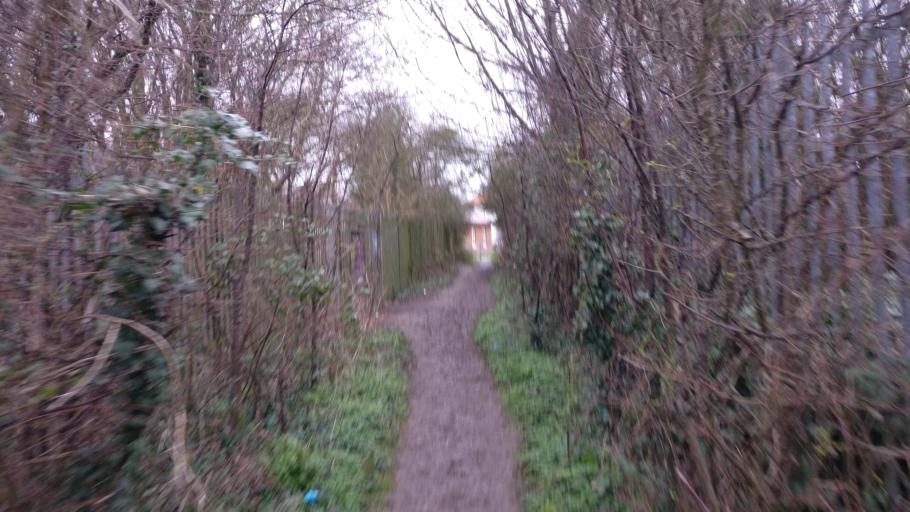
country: GB
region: England
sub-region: Hampshire
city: Basingstoke
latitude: 51.2593
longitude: -1.1422
